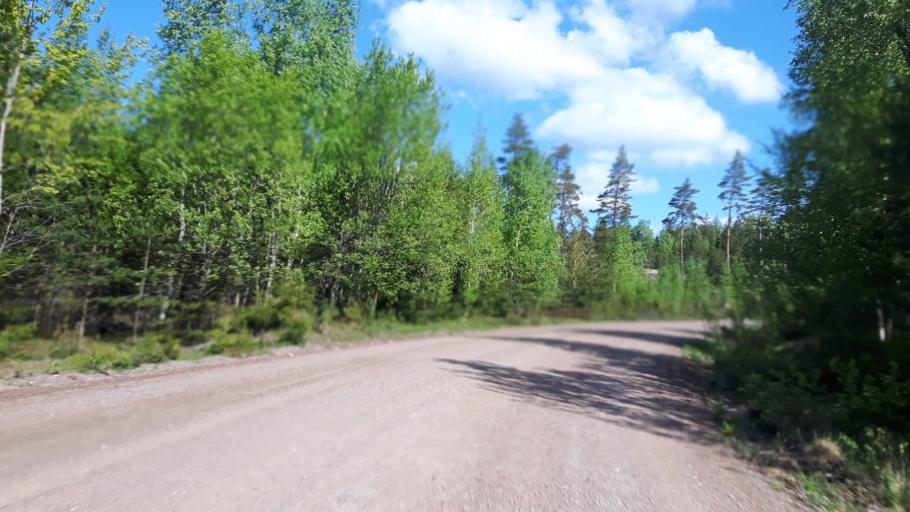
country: FI
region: Kymenlaakso
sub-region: Kotka-Hamina
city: Hamina
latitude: 60.5270
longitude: 27.2836
